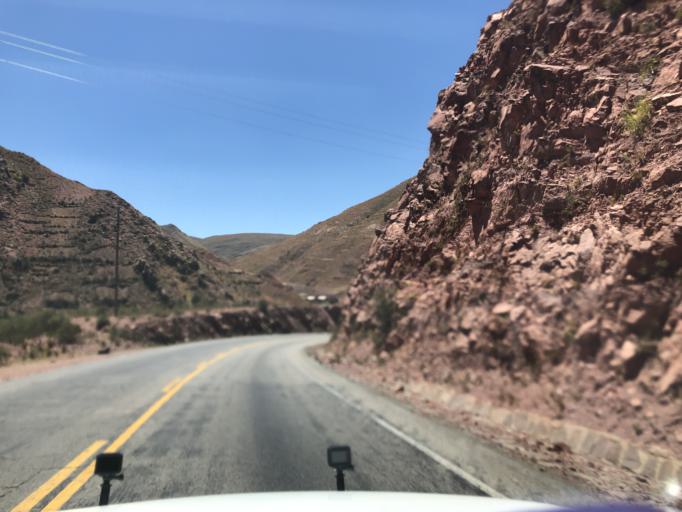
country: BO
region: Cochabamba
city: Irpa Irpa
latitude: -17.7192
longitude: -66.6119
